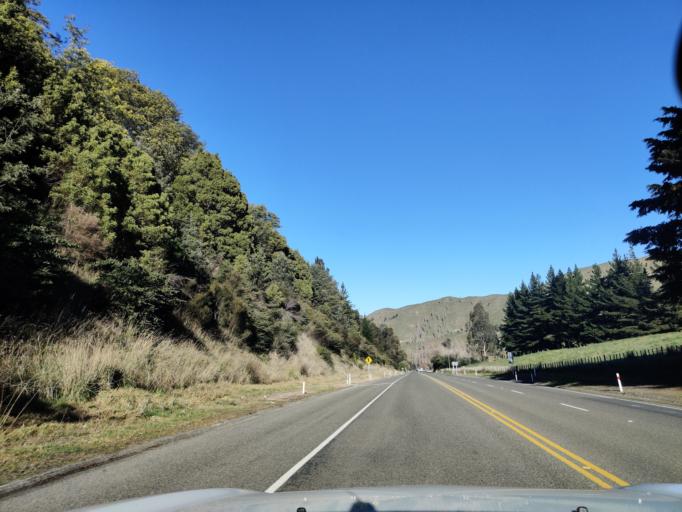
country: NZ
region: Manawatu-Wanganui
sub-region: Ruapehu District
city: Waiouru
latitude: -39.7709
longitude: 175.7969
